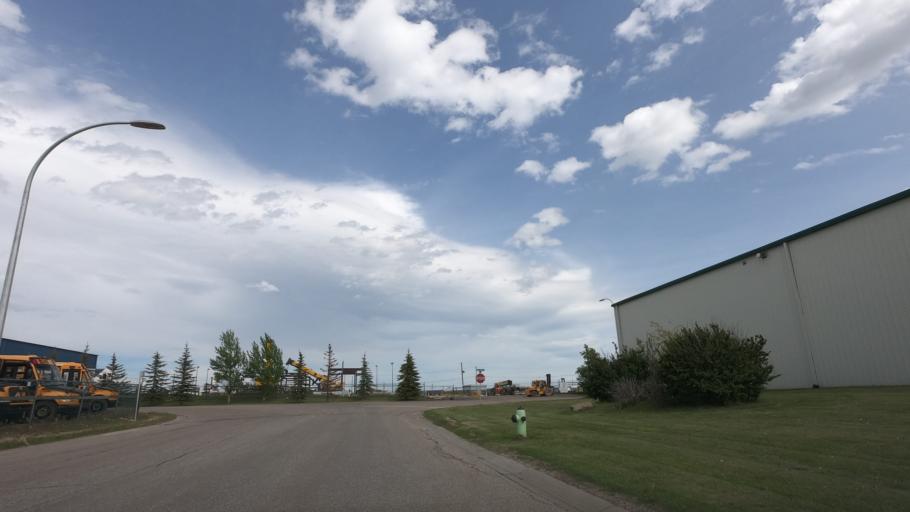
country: CA
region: Alberta
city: Airdrie
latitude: 51.2918
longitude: -113.9814
